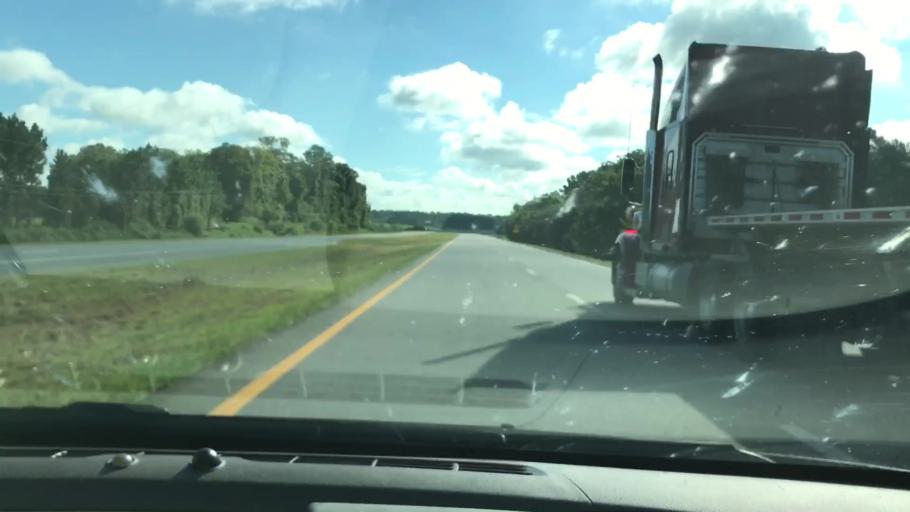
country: US
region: Georgia
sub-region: Worth County
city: Sylvester
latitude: 31.5513
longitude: -83.9575
